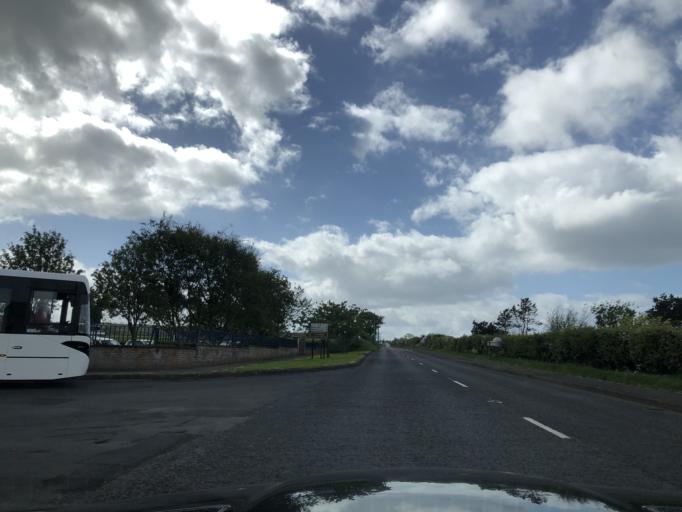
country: GB
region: Northern Ireland
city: Bushmills
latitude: 55.2062
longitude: -6.5307
